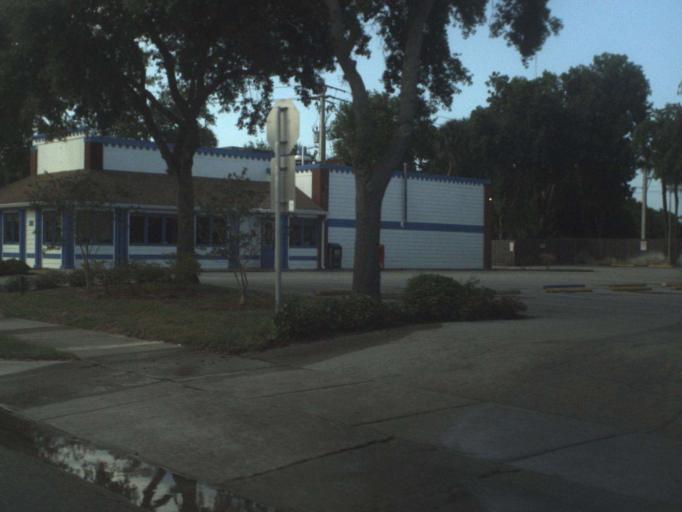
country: US
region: Florida
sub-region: Volusia County
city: South Daytona
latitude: 29.1856
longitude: -81.0093
